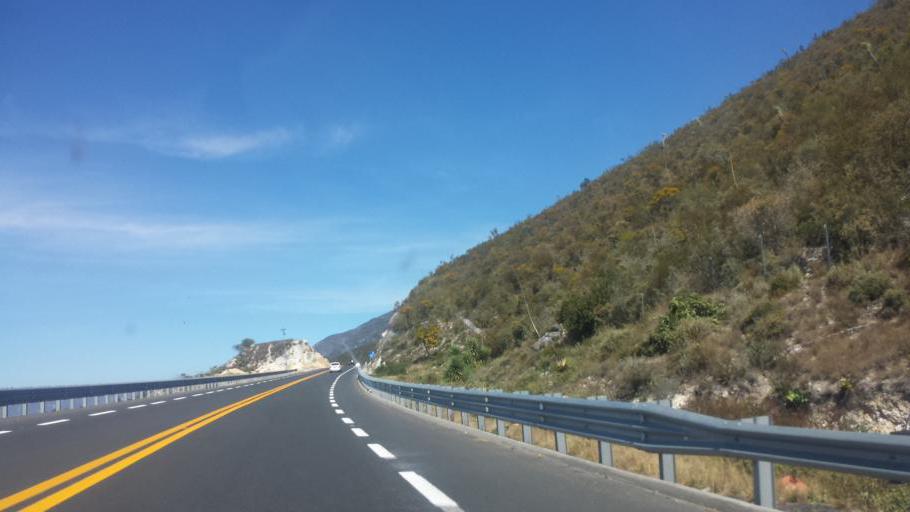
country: MX
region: Puebla
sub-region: San Jose Miahuatlan
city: San Pedro Tetitlan
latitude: 18.0085
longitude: -97.3558
